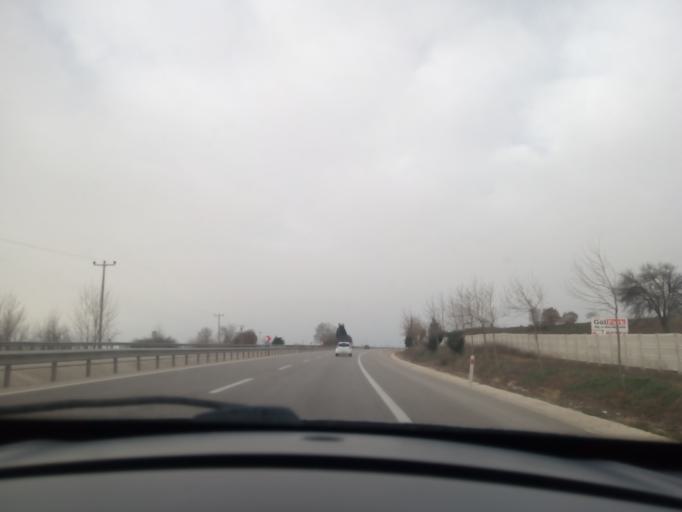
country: TR
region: Bursa
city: Mahmudiye
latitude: 40.2087
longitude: 28.6012
